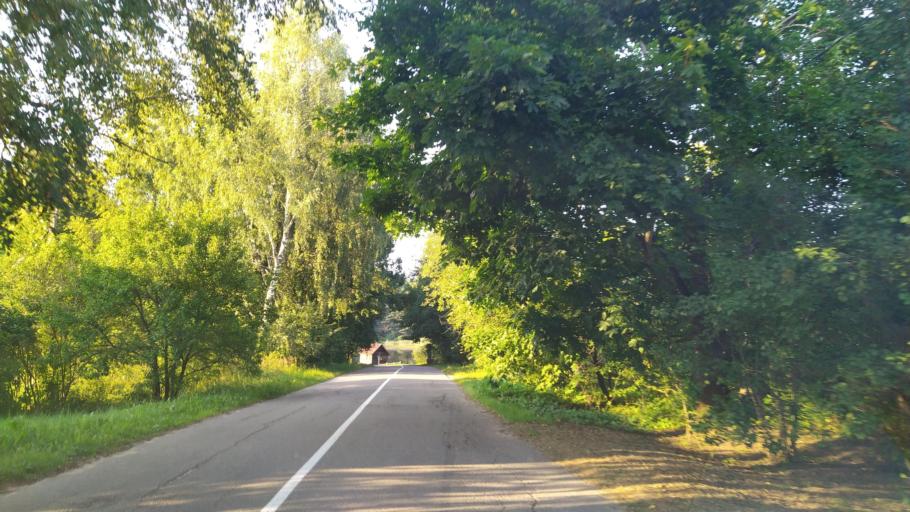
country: RU
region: Pskov
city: Pushkinskiye Gory
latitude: 57.0451
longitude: 28.9174
